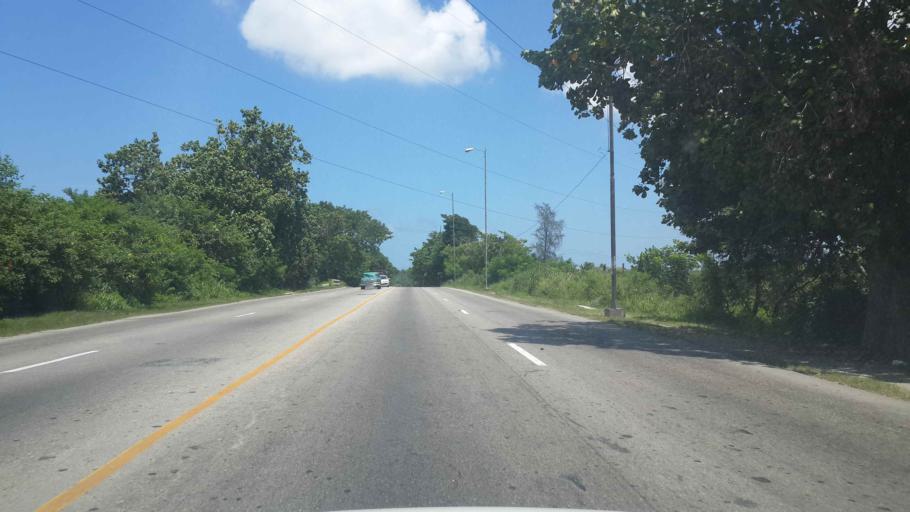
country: CU
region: La Habana
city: Guanabacoa
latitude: 23.1383
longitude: -82.3062
